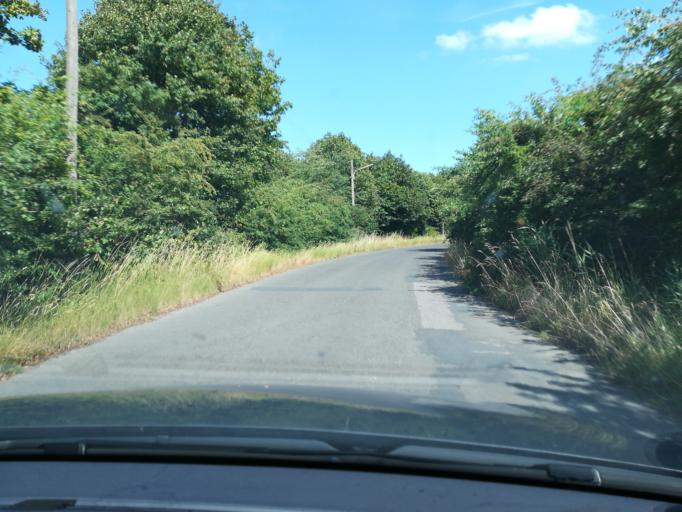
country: DE
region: Hamburg
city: Rothenburgsort
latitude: 53.4945
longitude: 10.0302
